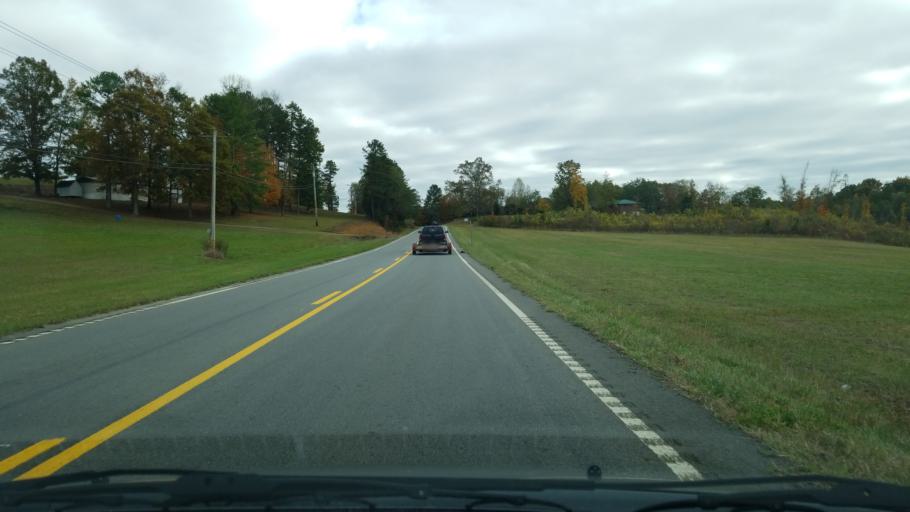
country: US
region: Tennessee
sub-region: Bradley County
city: Hopewell
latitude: 35.3259
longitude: -84.9691
